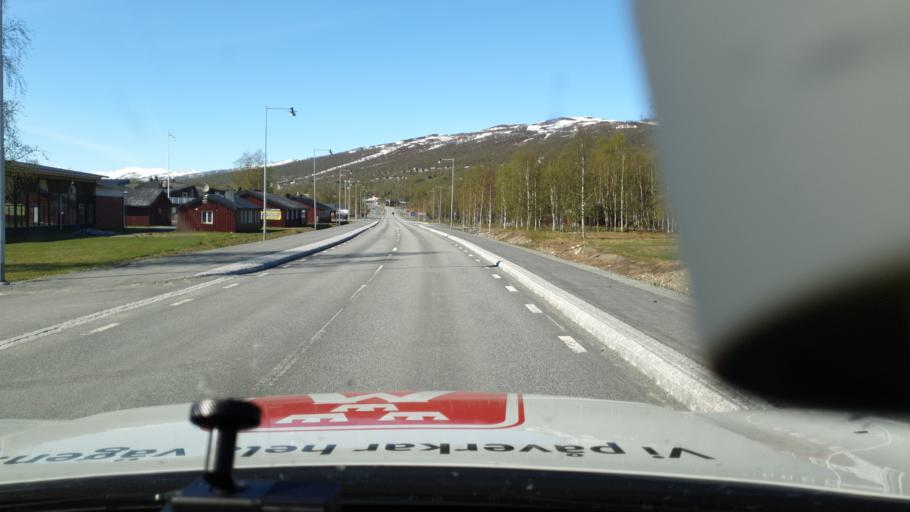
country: NO
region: Nordland
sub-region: Rana
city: Mo i Rana
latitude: 65.8106
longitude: 15.0886
